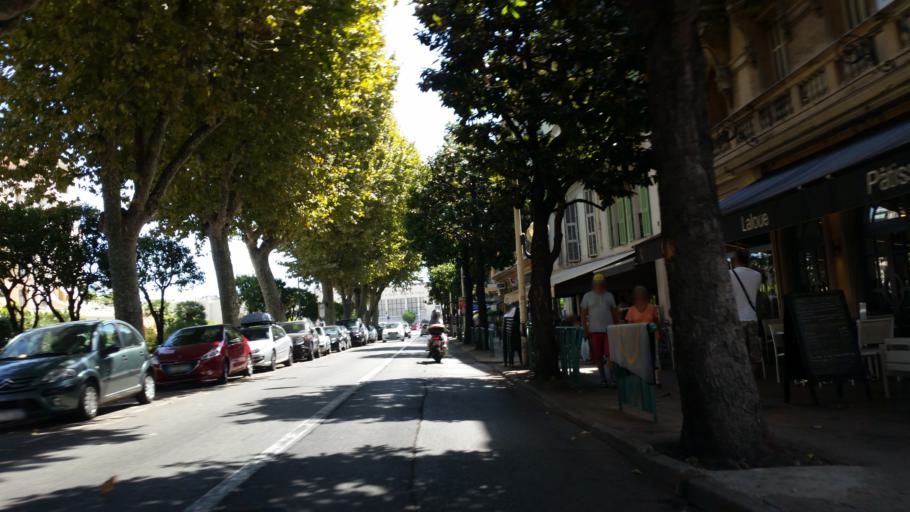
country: FR
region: Provence-Alpes-Cote d'Azur
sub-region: Departement des Alpes-Maritimes
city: Menton
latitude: 43.7739
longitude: 7.4971
